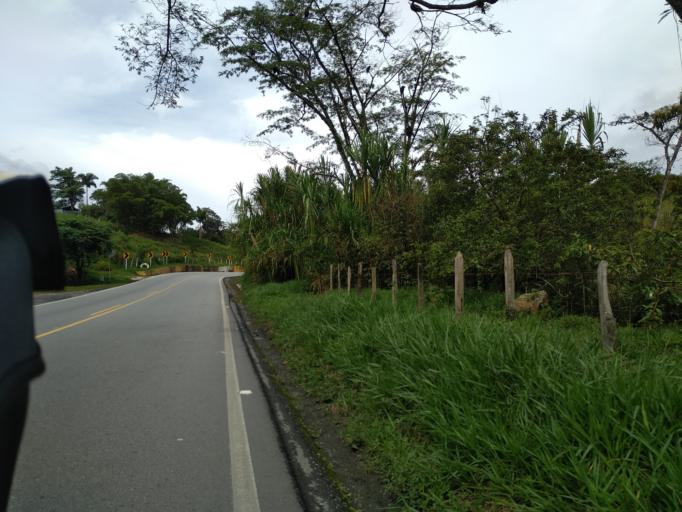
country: CO
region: Santander
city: Suaita
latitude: 6.0988
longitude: -73.3725
